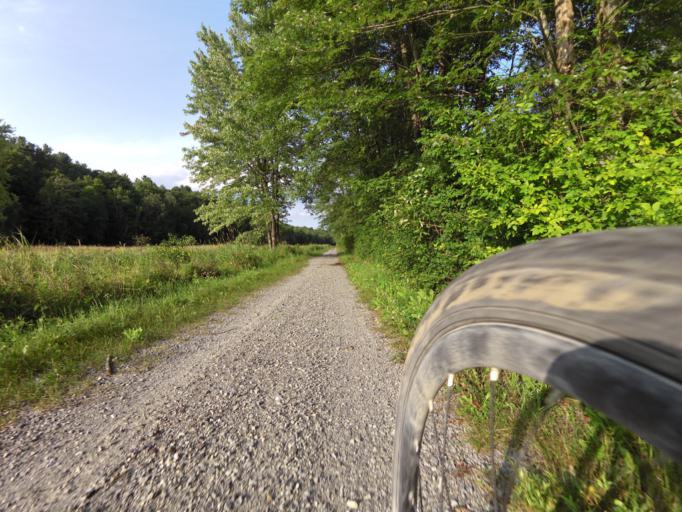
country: CA
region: Ontario
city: Kingston
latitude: 44.5029
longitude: -76.4373
